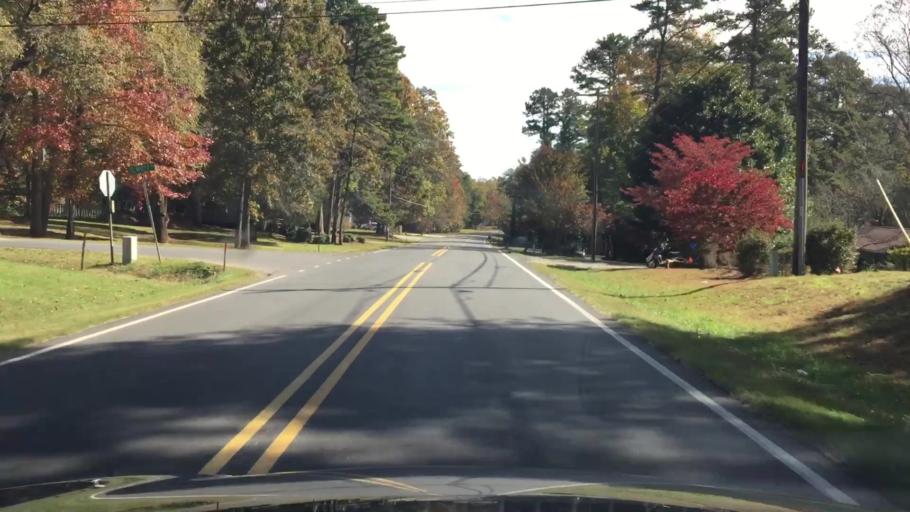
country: US
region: North Carolina
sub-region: Gaston County
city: Davidson
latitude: 35.5375
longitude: -80.8320
